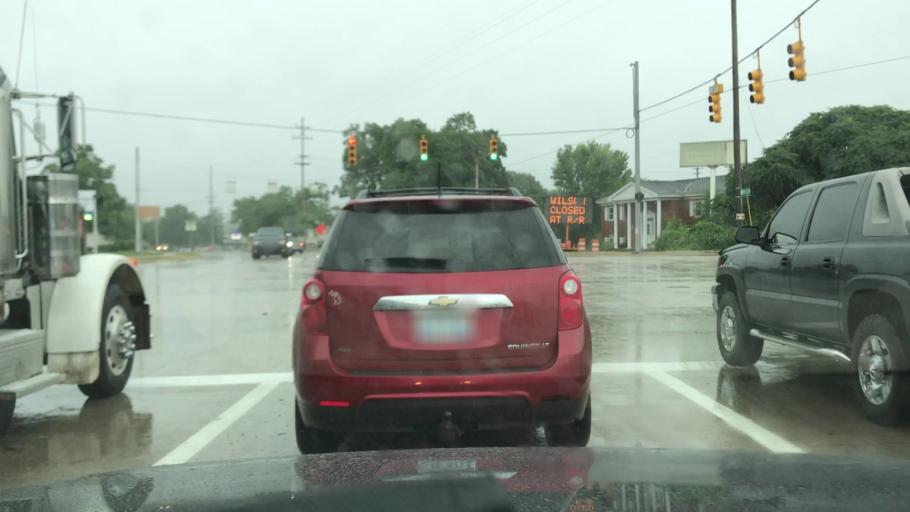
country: US
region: Michigan
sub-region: Kent County
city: Grandville
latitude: 42.9139
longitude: -85.7631
